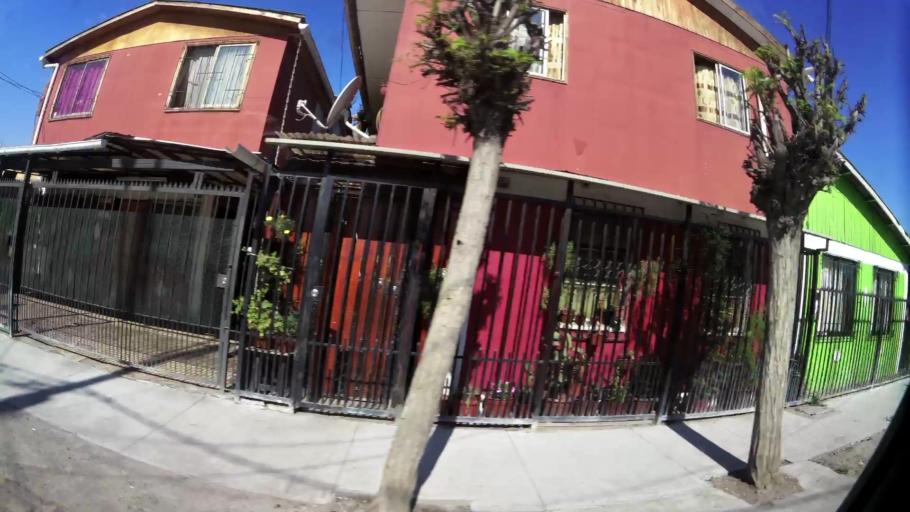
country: CL
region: Santiago Metropolitan
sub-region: Provincia de Santiago
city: Lo Prado
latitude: -33.5131
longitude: -70.6973
